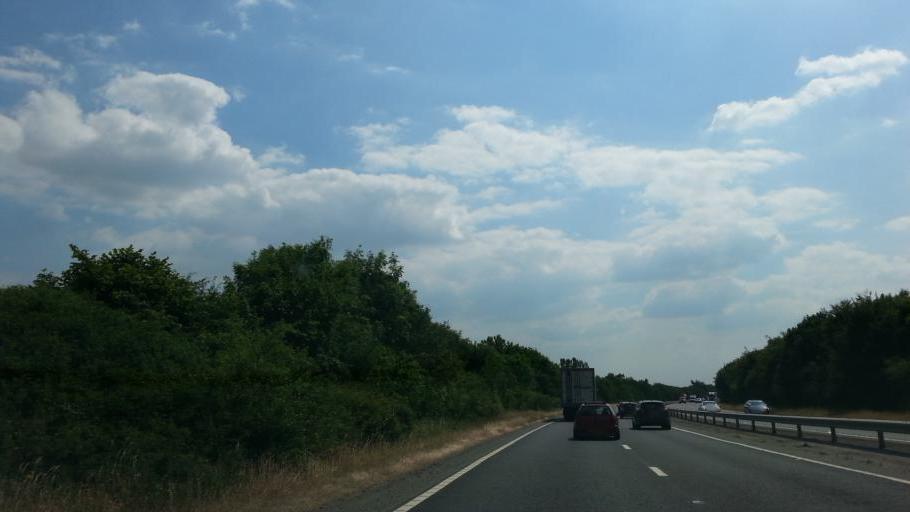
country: GB
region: England
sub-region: Cambridgeshire
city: Isleham
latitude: 52.2975
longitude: 0.4765
